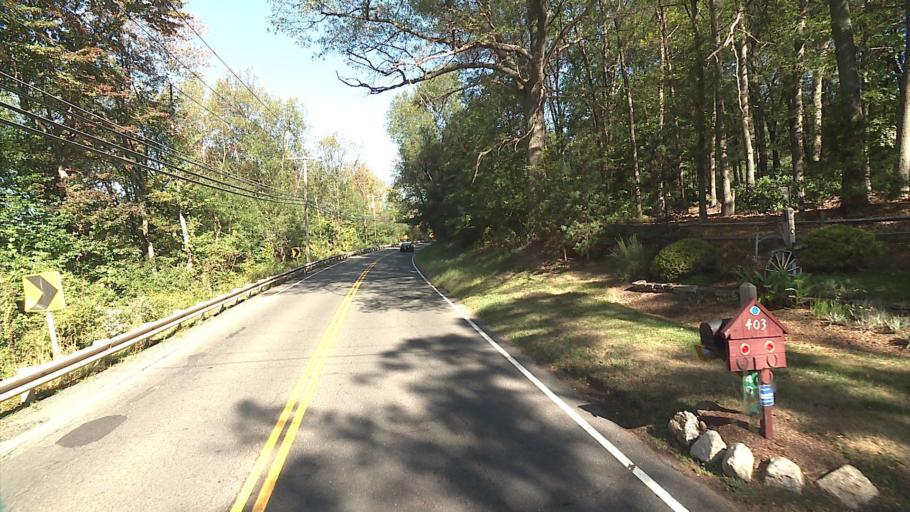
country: US
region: Connecticut
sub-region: Tolland County
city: Ellington
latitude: 41.9292
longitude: -72.4559
